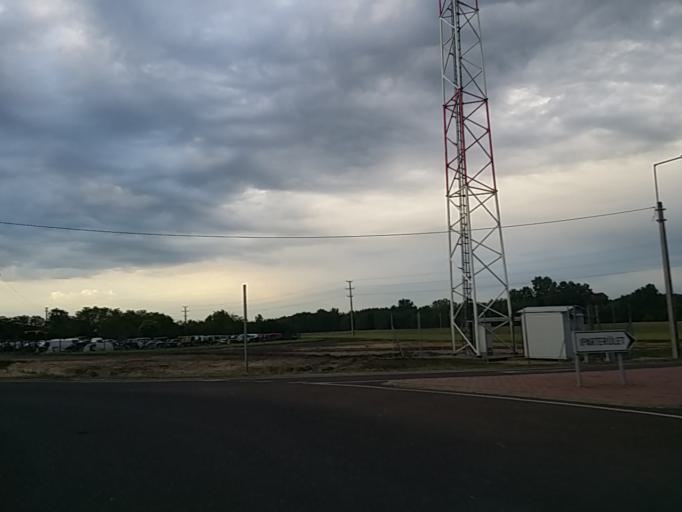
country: HU
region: Pest
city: Taborfalva
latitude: 47.0911
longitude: 19.4774
